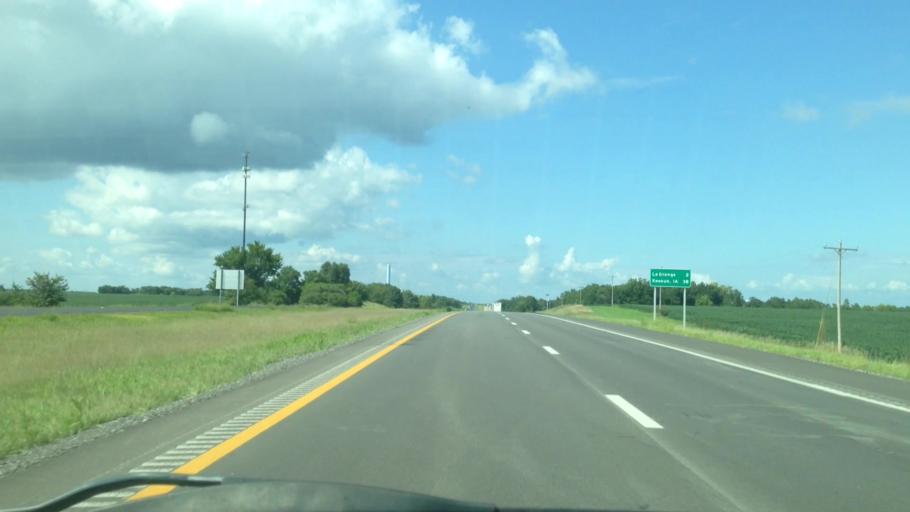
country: US
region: Illinois
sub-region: Adams County
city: Quincy
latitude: 40.0194
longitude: -91.5260
